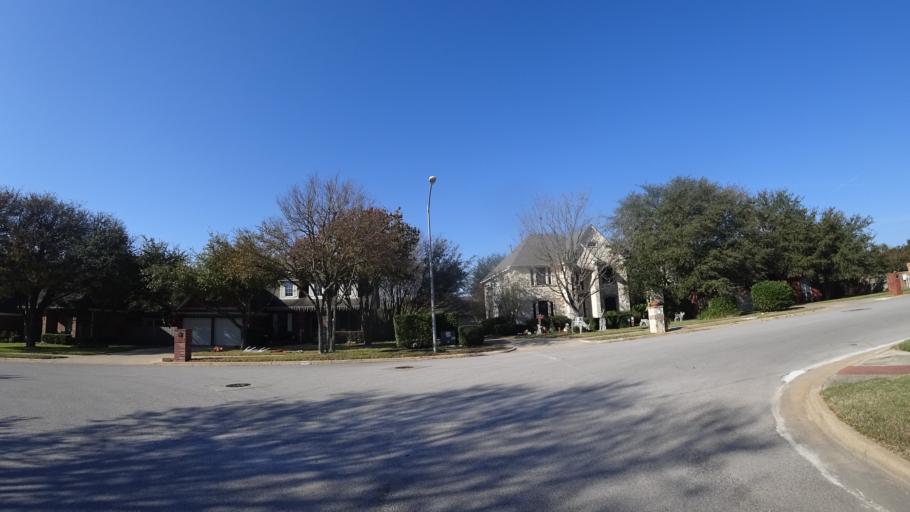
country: US
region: Texas
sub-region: Travis County
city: Shady Hollow
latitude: 30.2243
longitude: -97.8519
